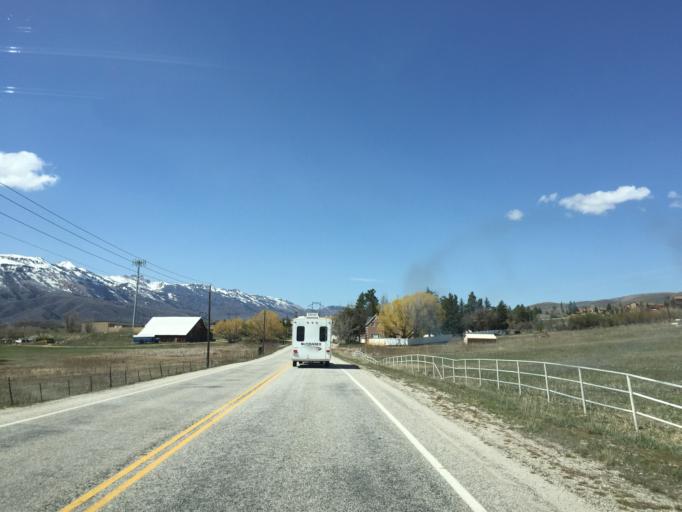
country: US
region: Utah
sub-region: Weber County
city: Wolf Creek
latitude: 41.3181
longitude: -111.8267
